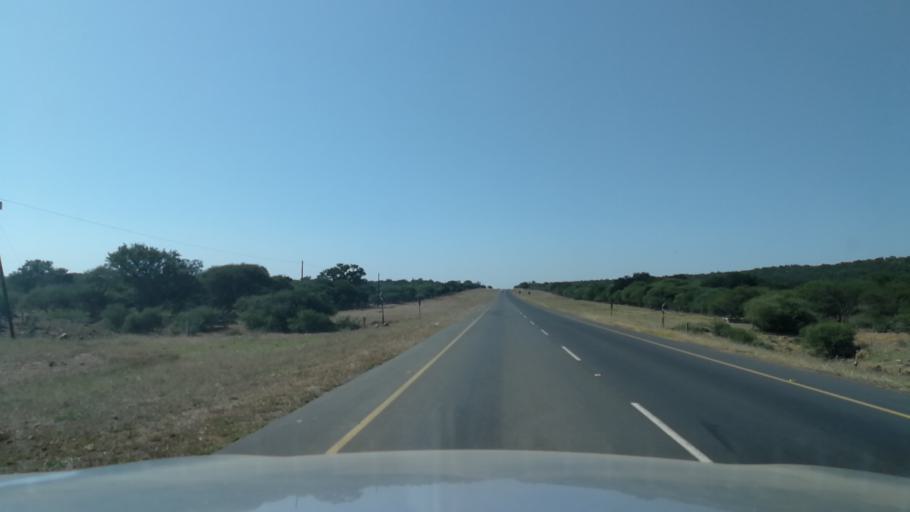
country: BW
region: South East
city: Ramotswa
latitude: -24.8145
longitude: 25.7765
